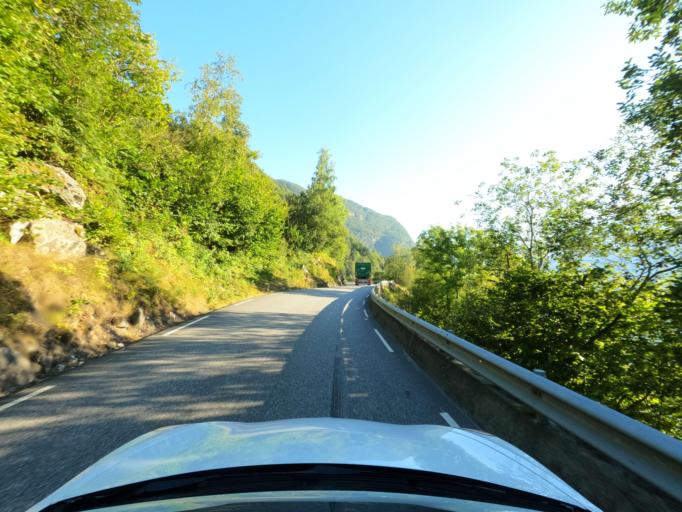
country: NO
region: Hordaland
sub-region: Odda
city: Odda
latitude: 60.1974
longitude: 6.5931
